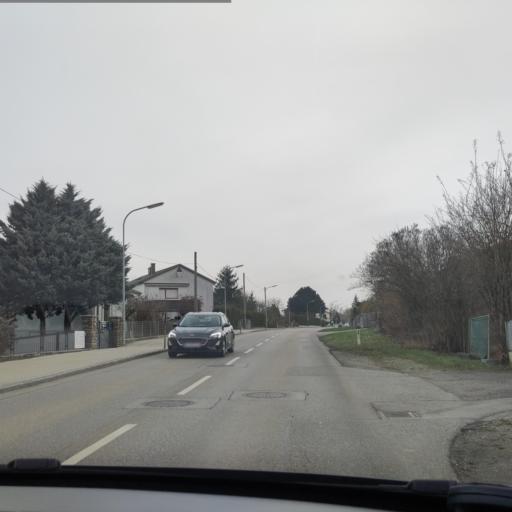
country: AT
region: Lower Austria
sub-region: Sankt Polten Stadt
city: Sankt Poelten
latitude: 48.2186
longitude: 15.6012
